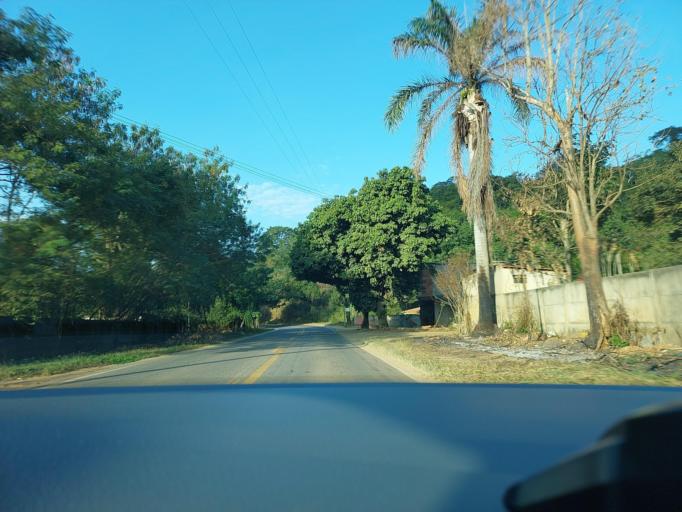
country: BR
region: Minas Gerais
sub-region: Muriae
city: Muriae
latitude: -21.1202
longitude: -42.4120
